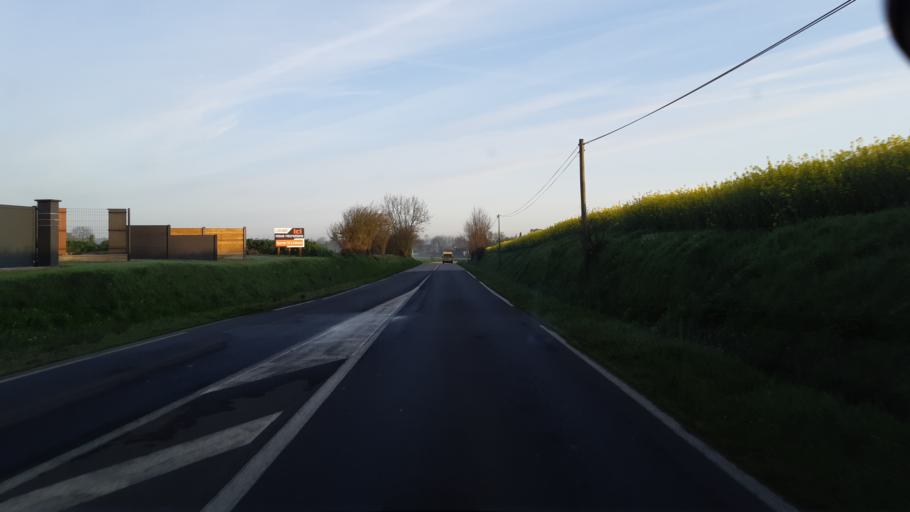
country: FR
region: Lower Normandy
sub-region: Departement de la Manche
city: Agneaux
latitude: 49.0533
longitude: -1.1308
